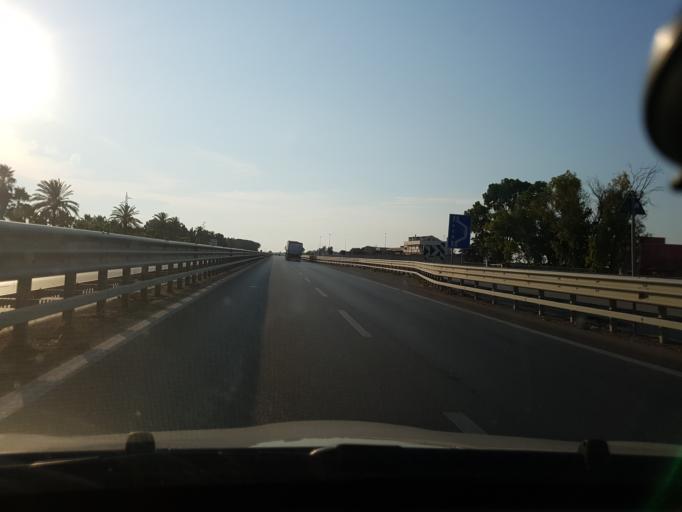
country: IT
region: Apulia
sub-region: Provincia di Foggia
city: Stornara
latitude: 41.3230
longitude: 15.7788
